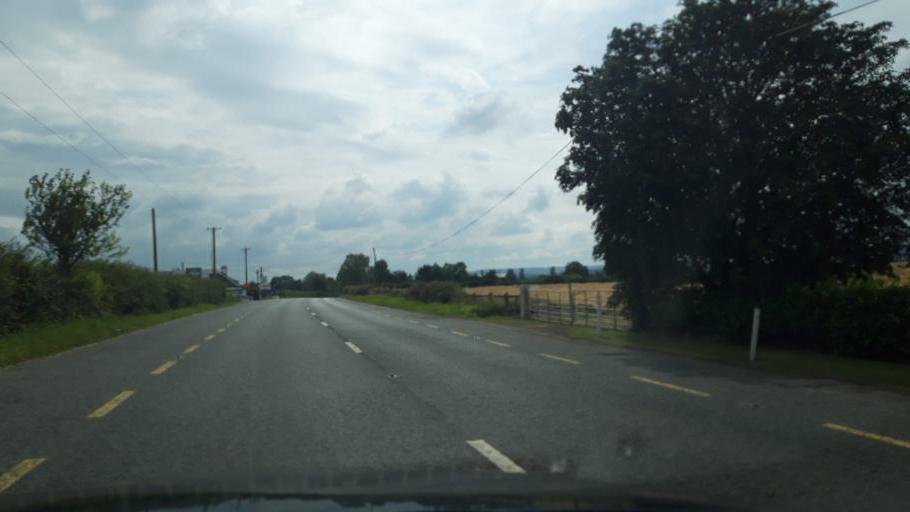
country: IE
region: Leinster
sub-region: Kildare
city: Athy
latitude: 52.9806
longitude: -7.0059
